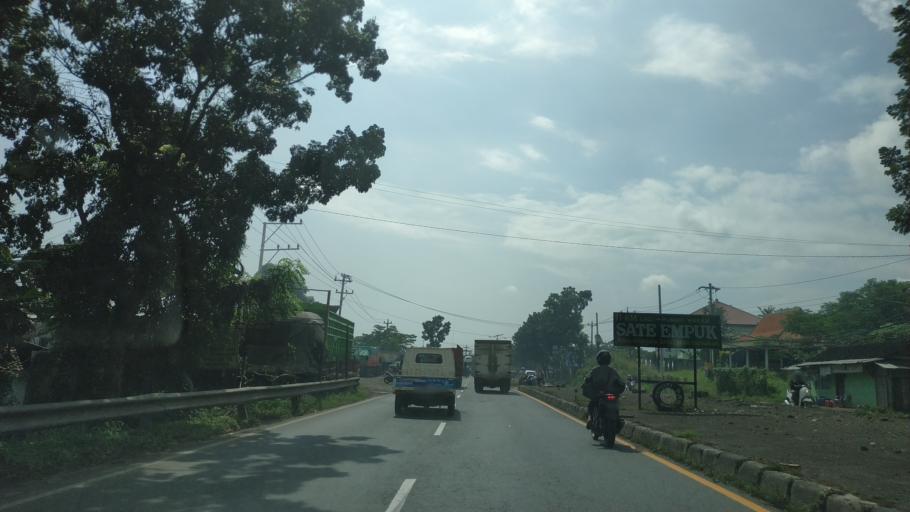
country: ID
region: Central Java
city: Pekalongan
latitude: -6.9251
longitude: 109.7594
